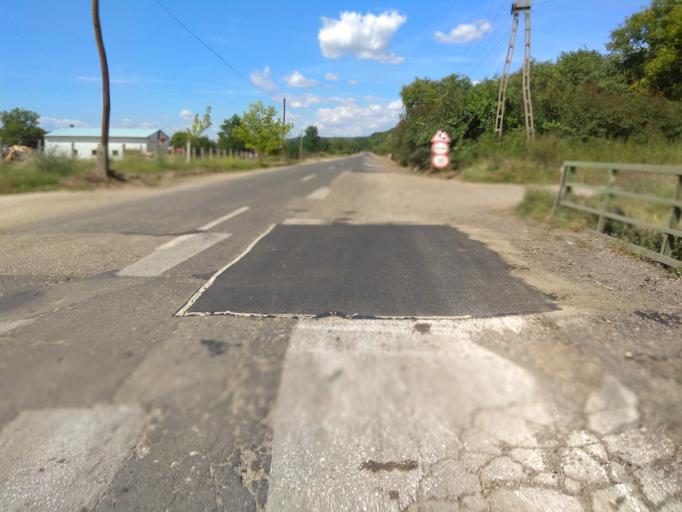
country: HU
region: Borsod-Abauj-Zemplen
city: Kazincbarcika
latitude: 48.2824
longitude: 20.6348
